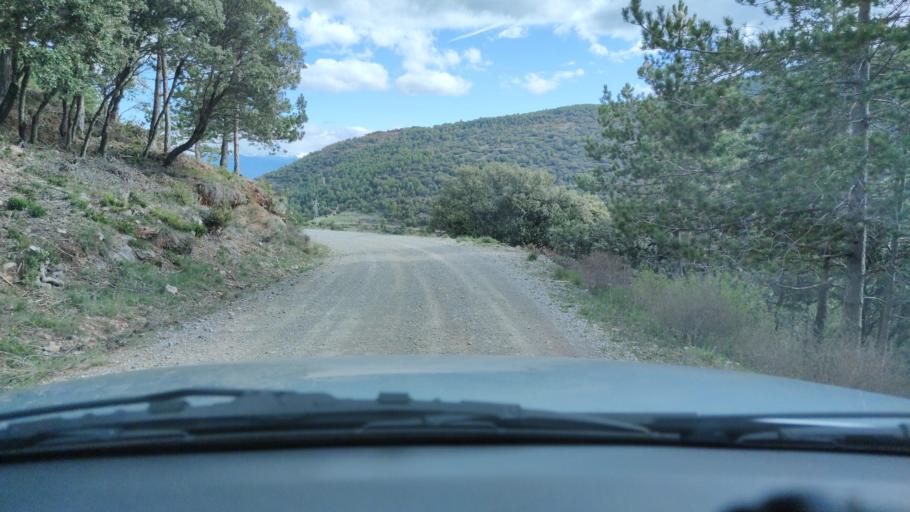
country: ES
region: Catalonia
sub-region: Provincia de Lleida
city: Coll de Nargo
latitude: 42.2460
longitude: 1.4086
